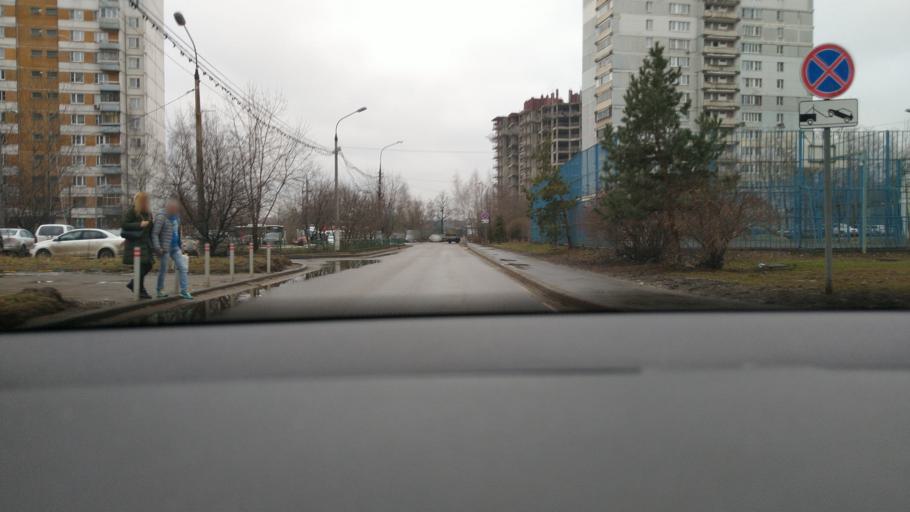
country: RU
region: Moskovskaya
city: Razvilka
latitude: 55.5878
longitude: 37.7565
